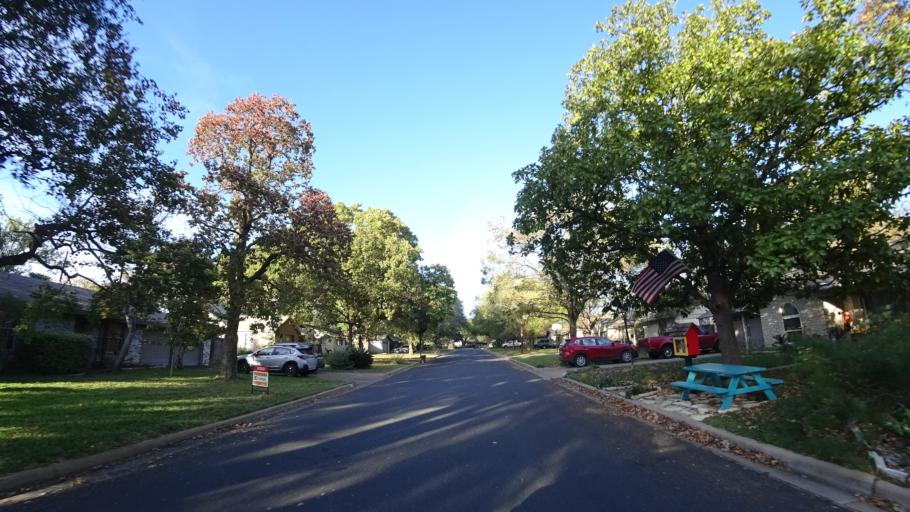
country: US
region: Texas
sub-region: Williamson County
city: Jollyville
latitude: 30.3698
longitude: -97.7307
